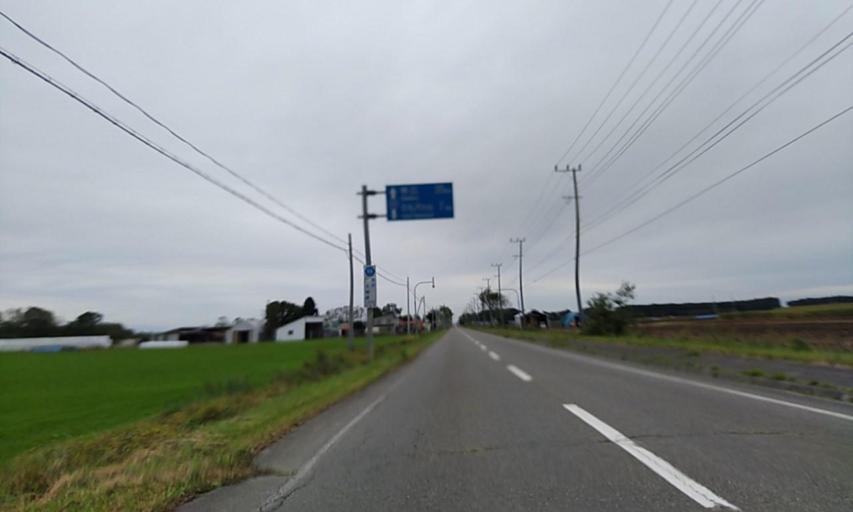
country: JP
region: Hokkaido
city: Obihiro
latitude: 42.6405
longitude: 143.0946
